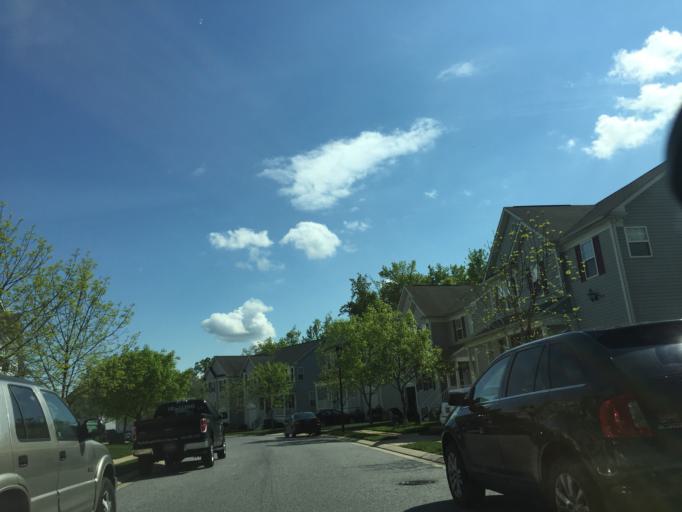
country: US
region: Maryland
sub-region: Baltimore County
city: Middle River
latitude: 39.3173
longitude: -76.4416
